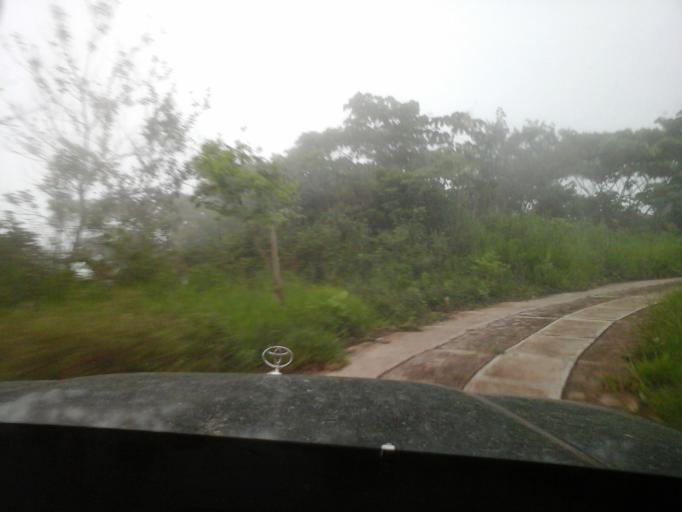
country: CO
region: Cesar
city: Agustin Codazzi
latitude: 9.9424
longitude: -73.1273
